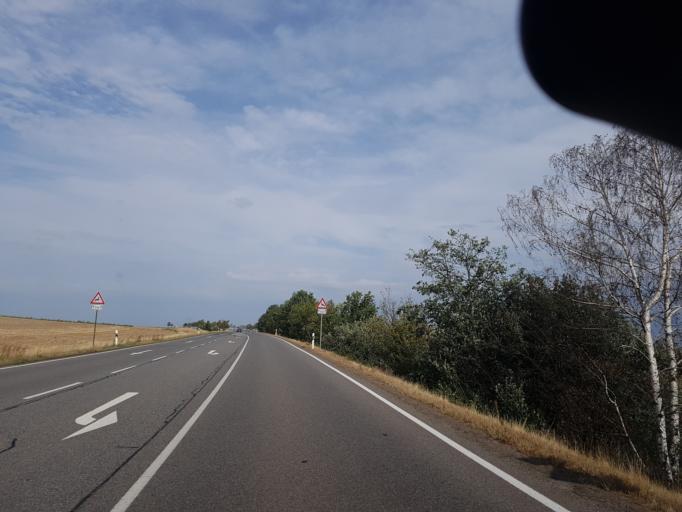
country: DE
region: Saxony
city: Hartha
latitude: 51.1128
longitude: 12.9901
